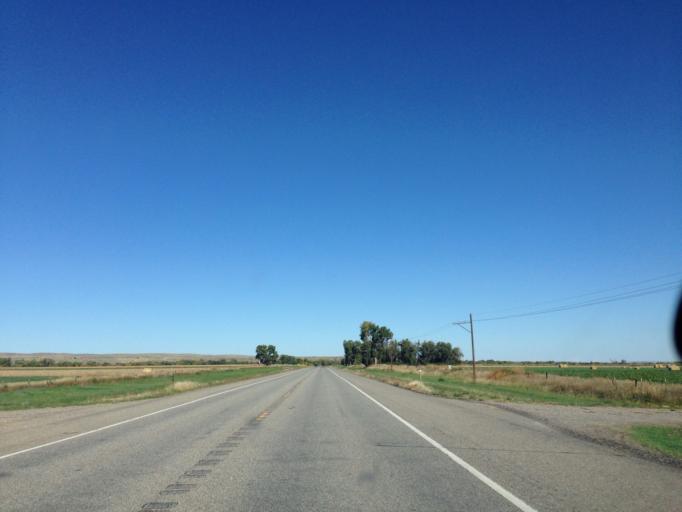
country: US
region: Montana
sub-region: Yellowstone County
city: Laurel
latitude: 45.5022
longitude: -108.8633
